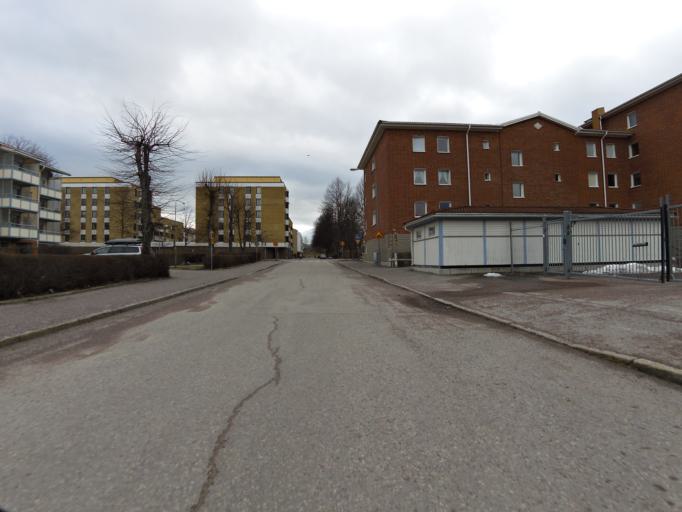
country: SE
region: Gaevleborg
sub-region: Gavle Kommun
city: Gavle
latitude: 60.6745
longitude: 17.1627
